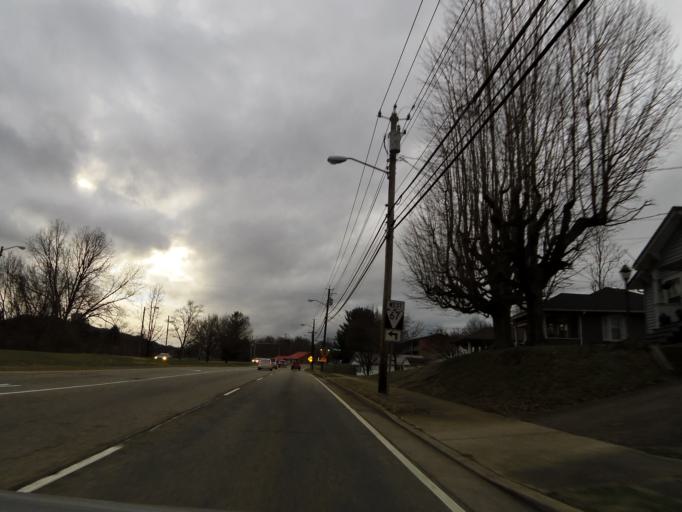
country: US
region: Tennessee
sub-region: Washington County
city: Johnson City
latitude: 36.3019
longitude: -82.3506
